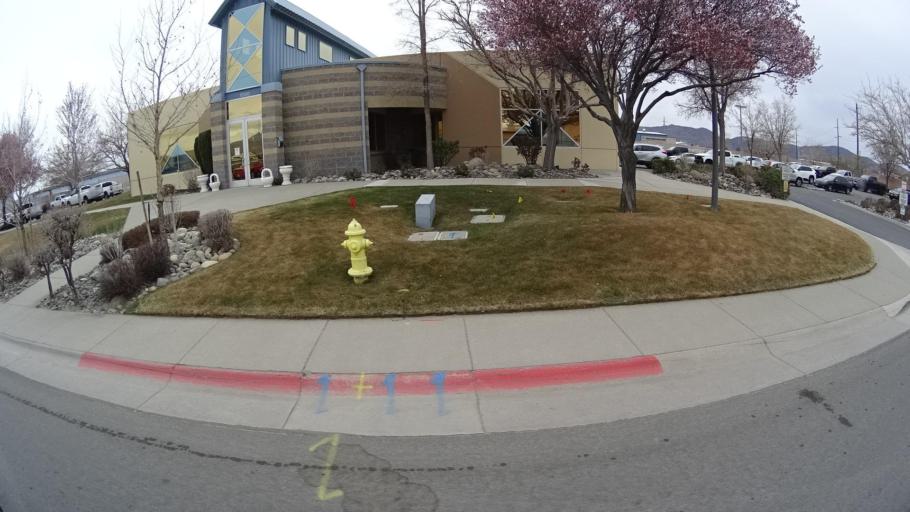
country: US
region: Nevada
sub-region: Washoe County
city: Sparks
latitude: 39.5241
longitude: -119.7714
